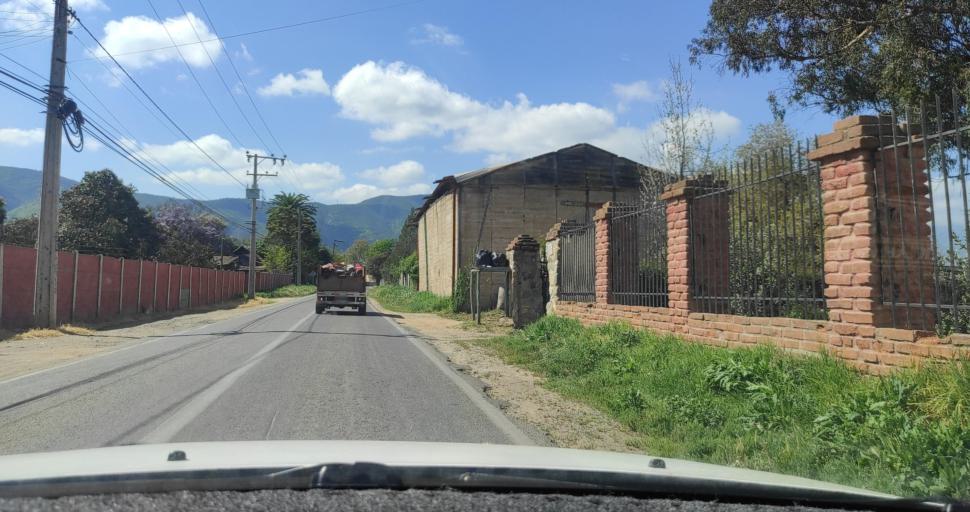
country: CL
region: Valparaiso
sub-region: Provincia de Marga Marga
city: Limache
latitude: -33.0052
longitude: -71.2393
